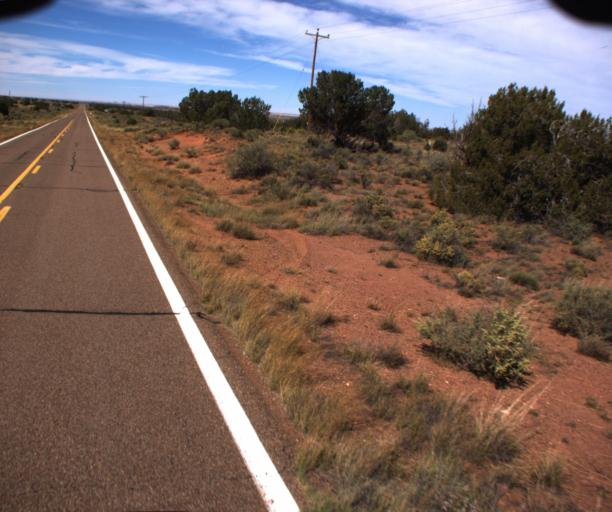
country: US
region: Arizona
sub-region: Apache County
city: Saint Johns
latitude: 34.6019
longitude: -109.6529
